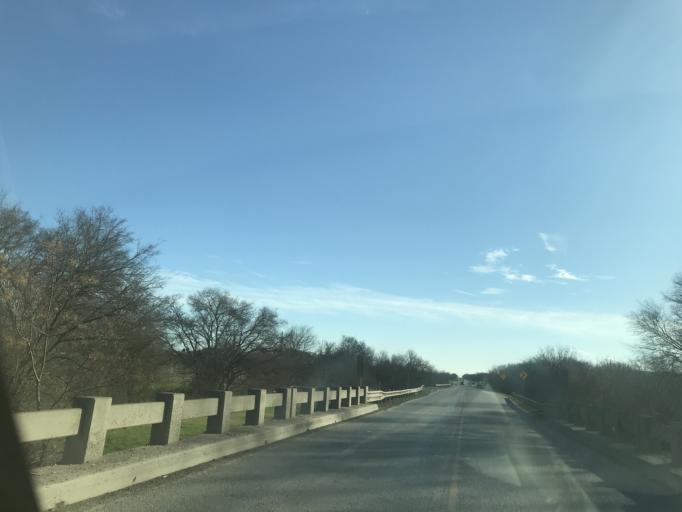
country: US
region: Texas
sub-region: Ellis County
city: Ferris
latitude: 32.5562
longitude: -96.6657
